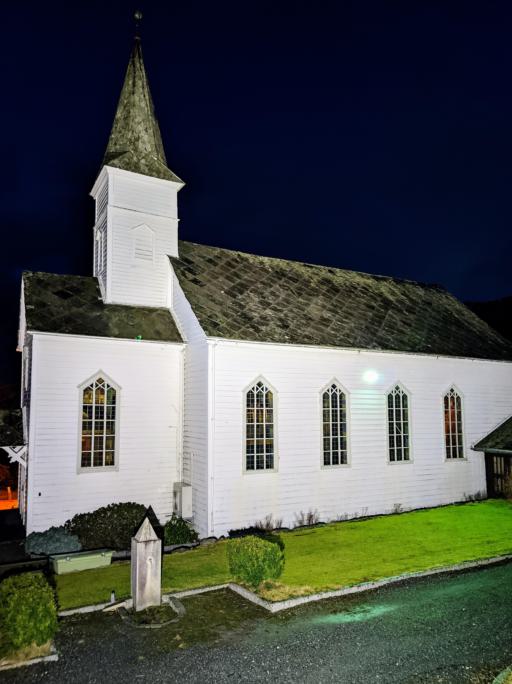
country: NO
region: Hordaland
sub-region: Tysnes
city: Uggdal
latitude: 59.8668
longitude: 5.7576
